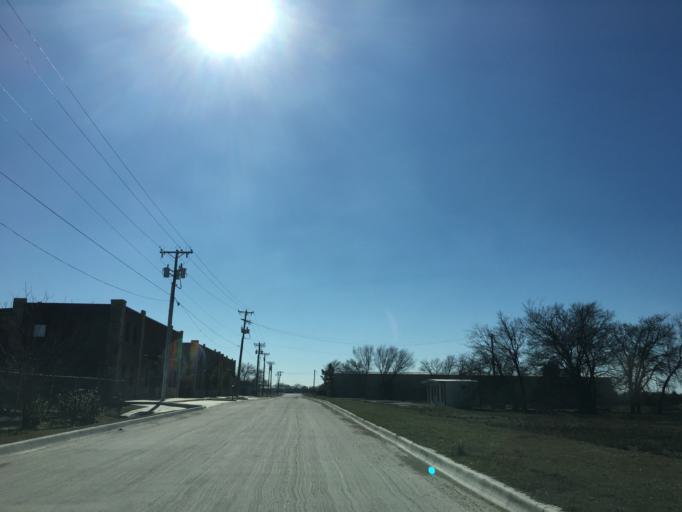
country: US
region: Texas
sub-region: Collin County
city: Prosper
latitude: 33.2361
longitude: -96.8058
